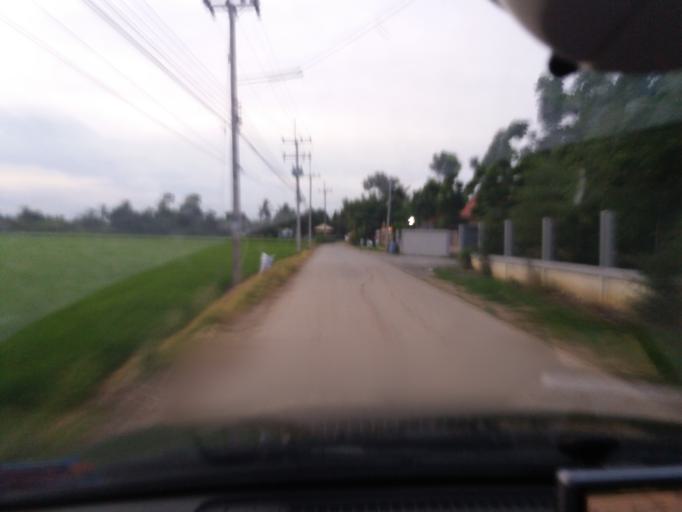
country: TH
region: Suphan Buri
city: Doembang Nangbuat
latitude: 14.8340
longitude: 100.1333
